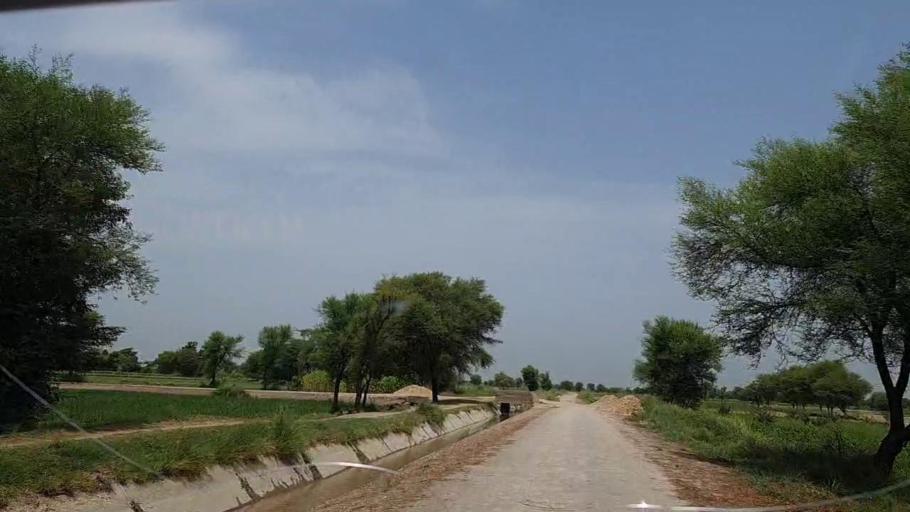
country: PK
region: Sindh
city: Tharu Shah
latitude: 26.9368
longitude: 68.0682
